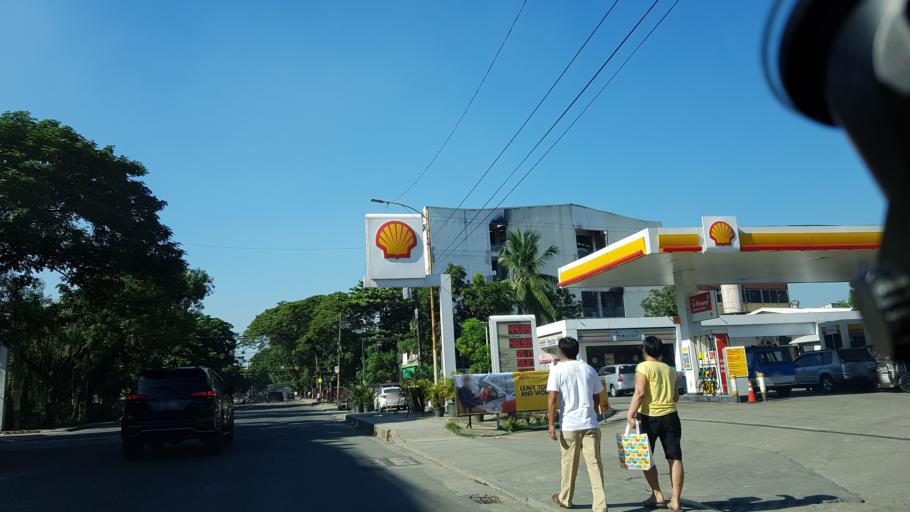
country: PH
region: Metro Manila
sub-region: Pasig
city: Pasig City
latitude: 14.5737
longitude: 121.0838
